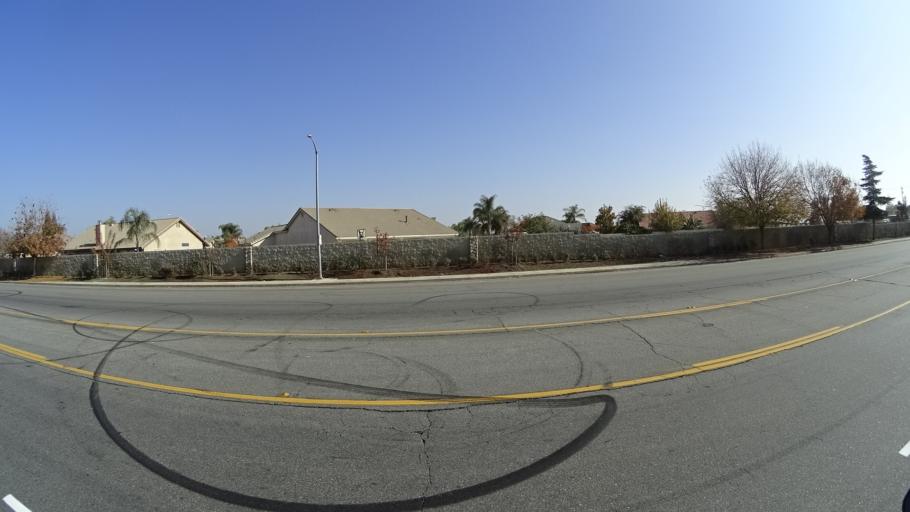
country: US
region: California
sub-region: Kern County
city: Greenfield
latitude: 35.2753
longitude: -119.0392
